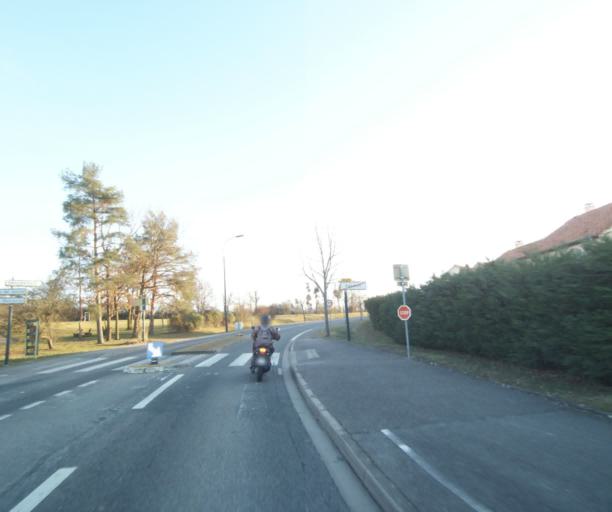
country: FR
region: Lorraine
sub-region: Departement de Meurthe-et-Moselle
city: Pulnoy
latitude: 48.6954
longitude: 6.2556
